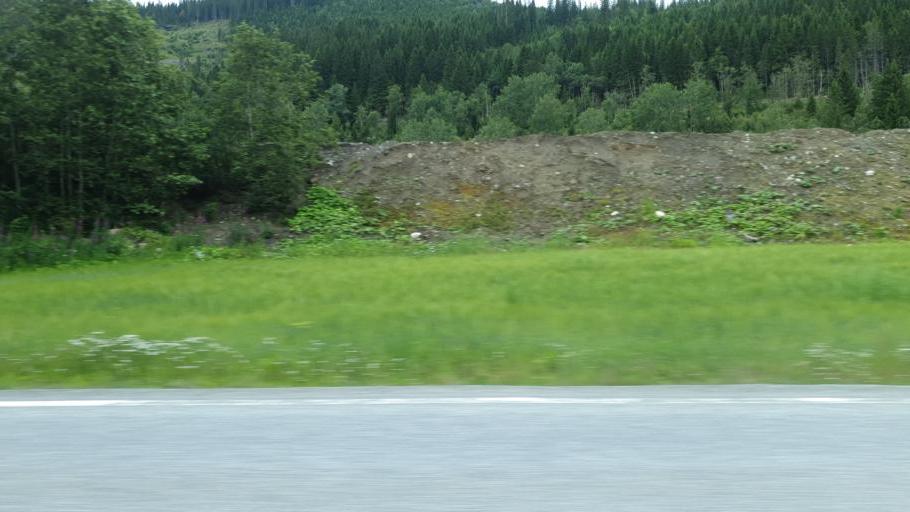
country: NO
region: Sor-Trondelag
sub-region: Midtre Gauldal
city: Storen
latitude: 63.0034
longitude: 10.2381
